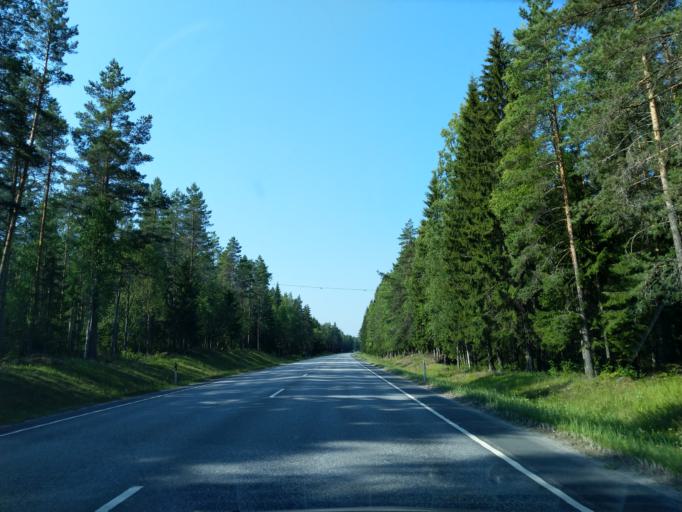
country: FI
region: Satakunta
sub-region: Pori
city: Noormarkku
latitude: 61.6282
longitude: 21.9252
